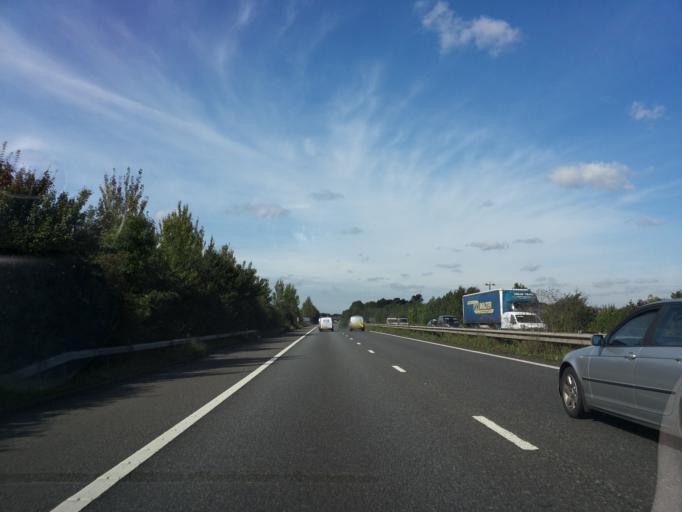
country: GB
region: England
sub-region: Kent
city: Sittingbourne
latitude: 51.3117
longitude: 0.7069
